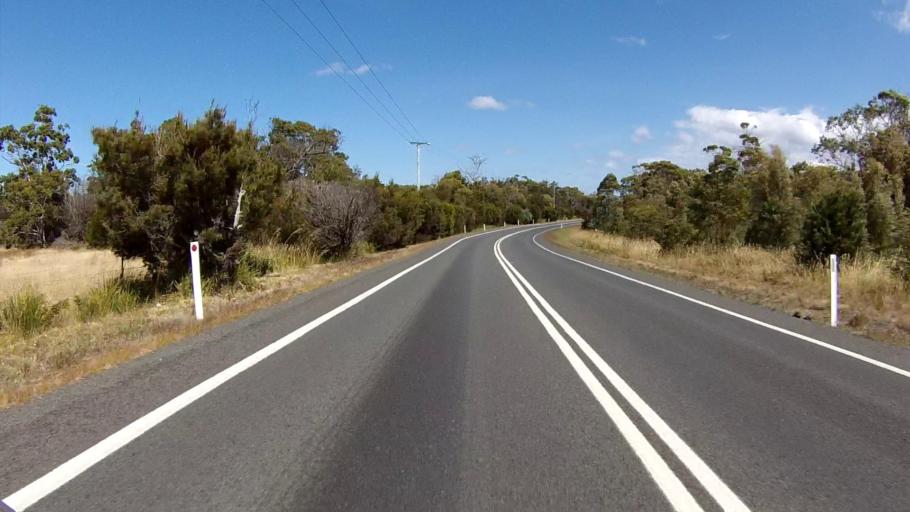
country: AU
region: Tasmania
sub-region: Break O'Day
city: St Helens
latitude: -42.0816
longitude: 148.0688
